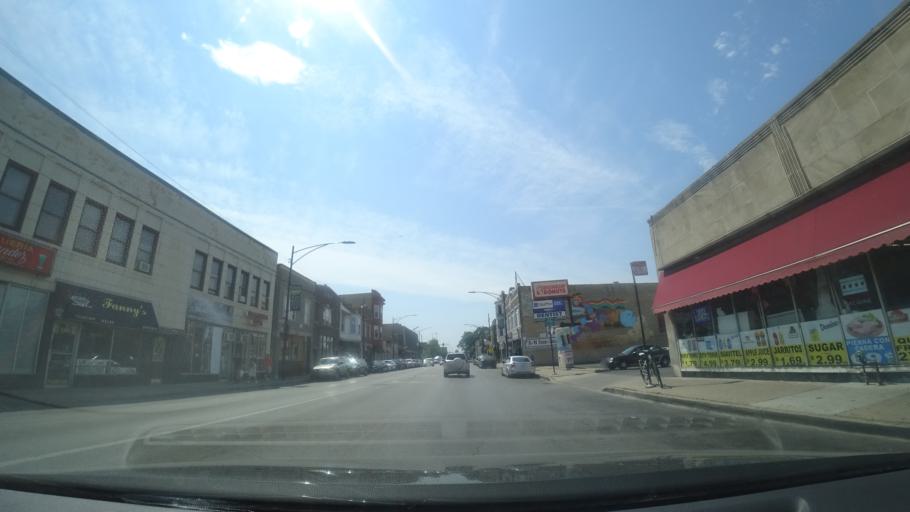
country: US
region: Illinois
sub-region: Cook County
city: Evanston
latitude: 42.0088
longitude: -87.6740
